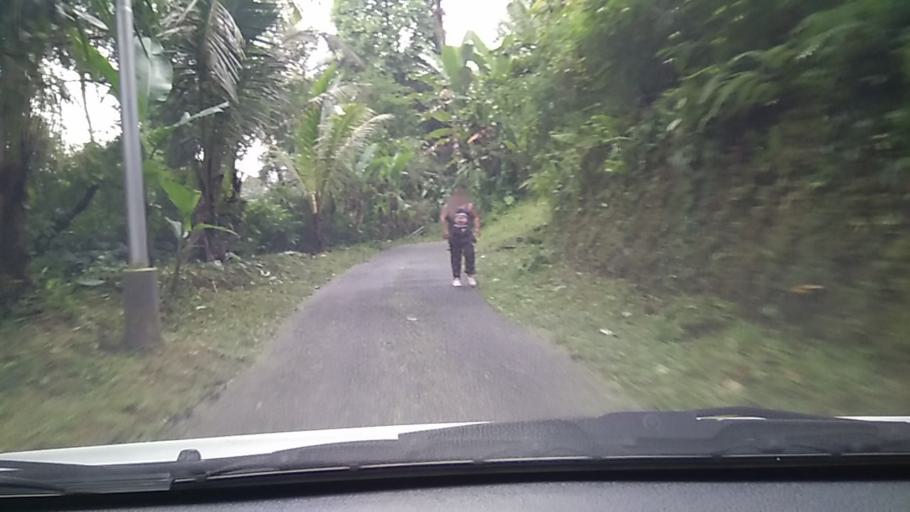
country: ID
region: Bali
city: Banjar Dujung Kaja
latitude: -8.4072
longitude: 115.2889
